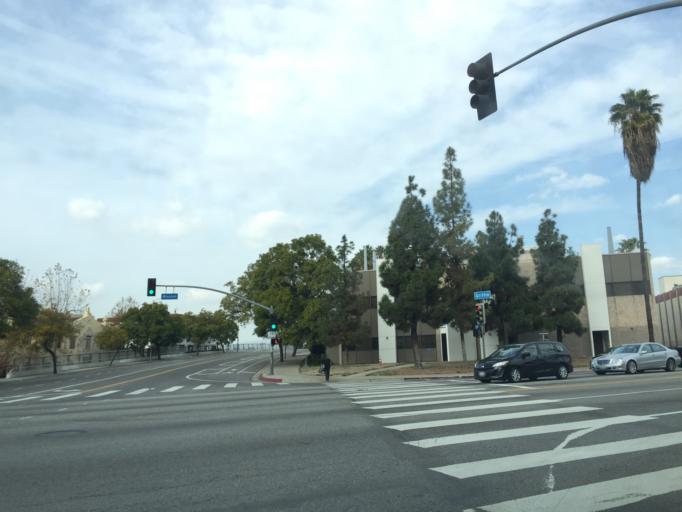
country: US
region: California
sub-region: Los Angeles County
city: Boyle Heights
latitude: 34.0627
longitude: -118.2111
